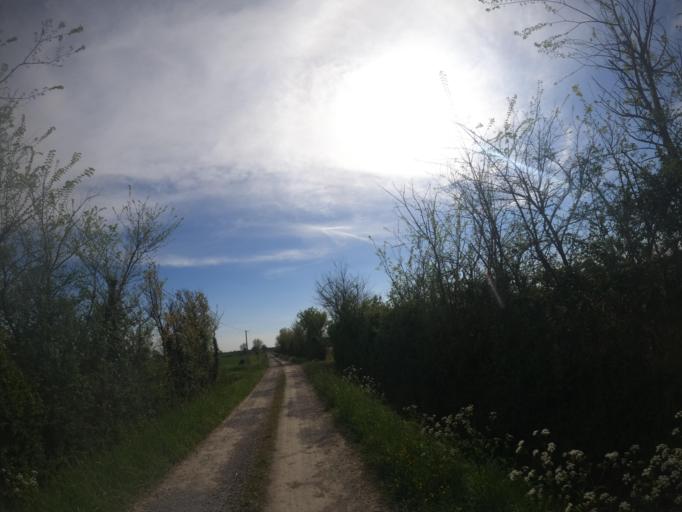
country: FR
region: Poitou-Charentes
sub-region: Departement des Deux-Sevres
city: Saint-Varent
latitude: 46.9220
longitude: -0.2418
